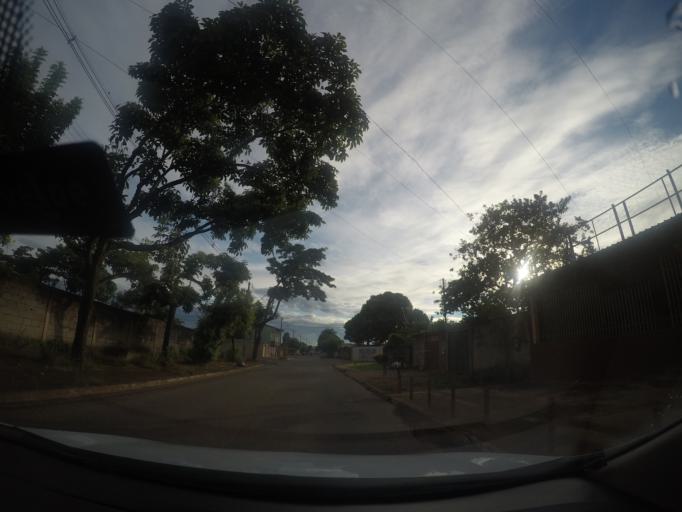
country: BR
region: Goias
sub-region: Goiania
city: Goiania
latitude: -16.6486
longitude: -49.3333
